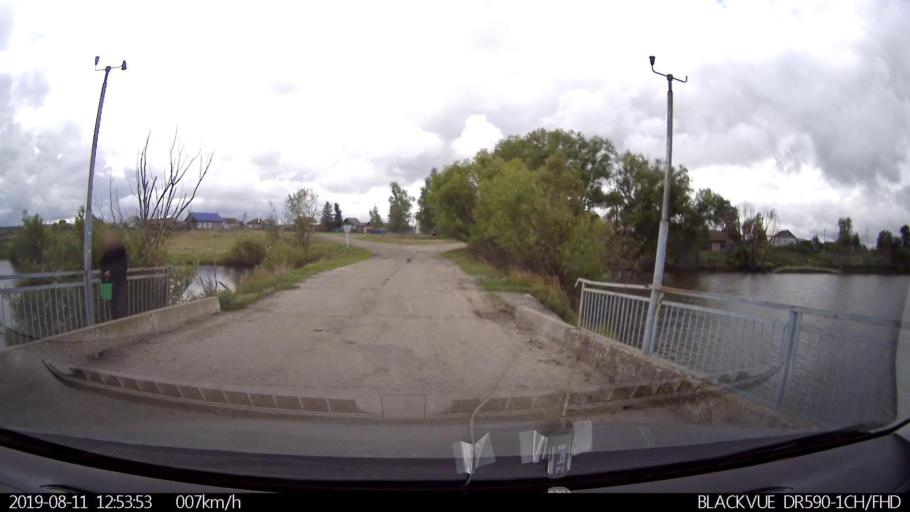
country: RU
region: Ulyanovsk
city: Ignatovka
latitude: 53.8746
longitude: 47.6500
